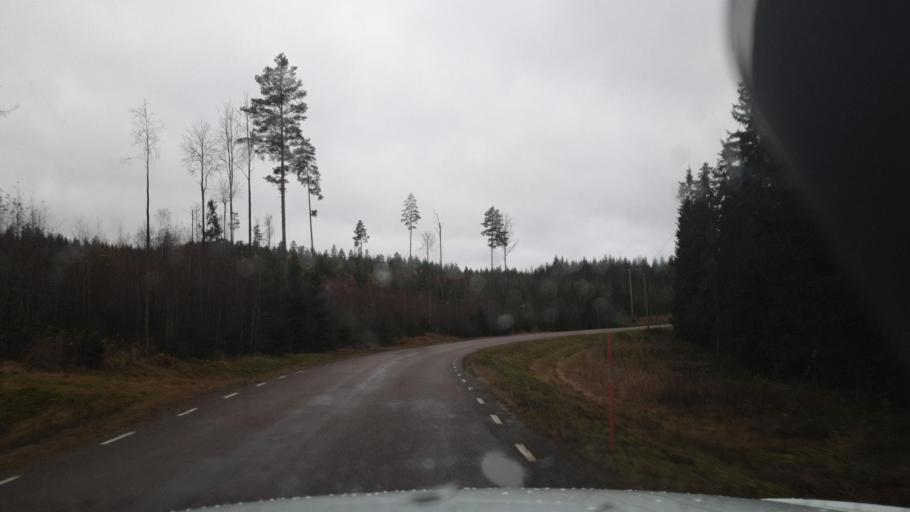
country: SE
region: Vaermland
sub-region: Eda Kommun
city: Charlottenberg
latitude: 59.9394
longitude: 12.3814
